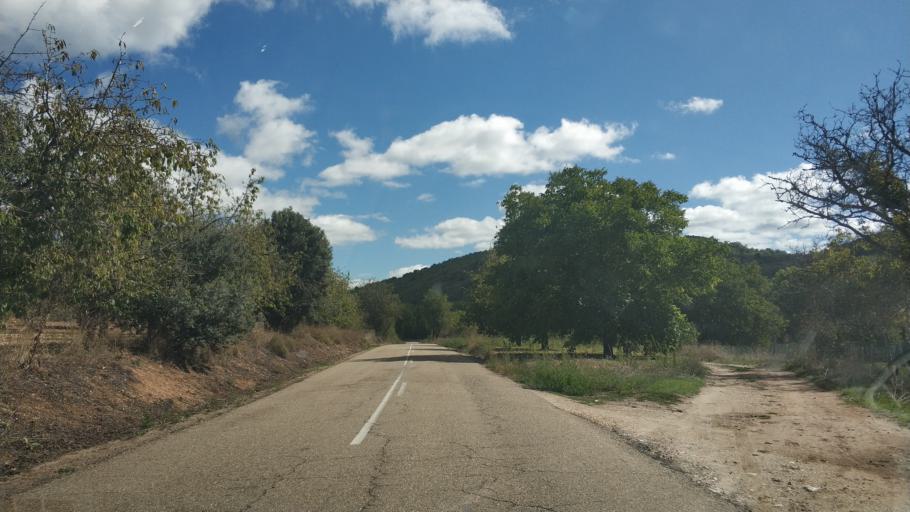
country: ES
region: Castille and Leon
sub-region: Provincia de Burgos
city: Covarrubias
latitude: 42.0562
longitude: -3.5115
